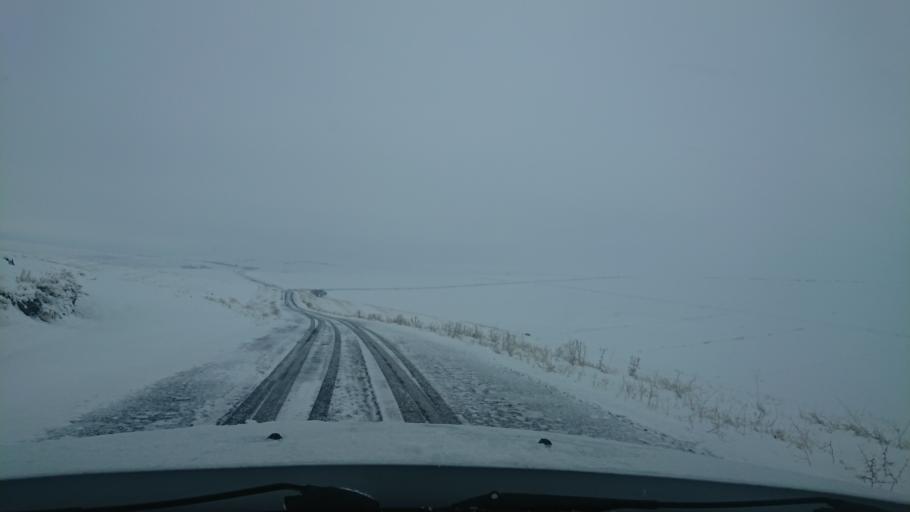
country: TR
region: Aksaray
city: Acipinar
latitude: 38.6668
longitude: 33.8533
